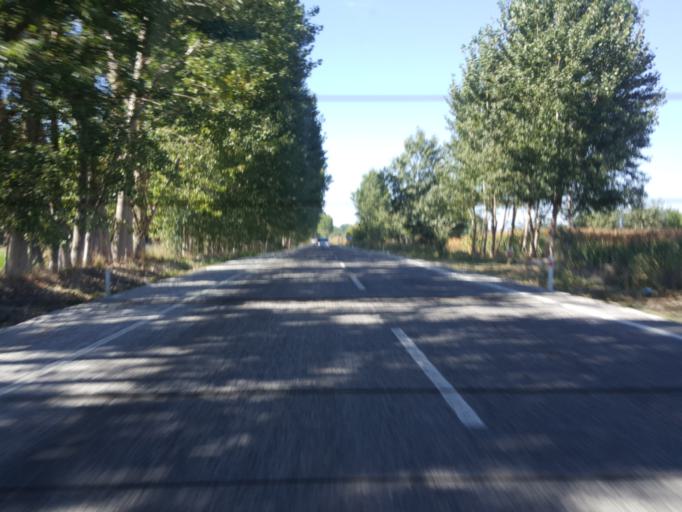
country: TR
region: Tokat
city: Pazar
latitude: 40.2692
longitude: 36.2228
